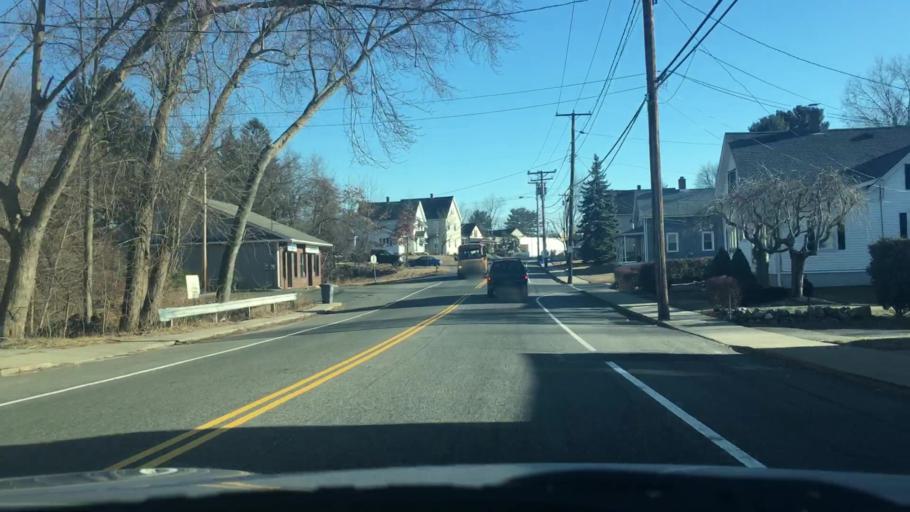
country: US
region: Massachusetts
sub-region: Hampden County
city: Ludlow
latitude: 42.1650
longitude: -72.4856
